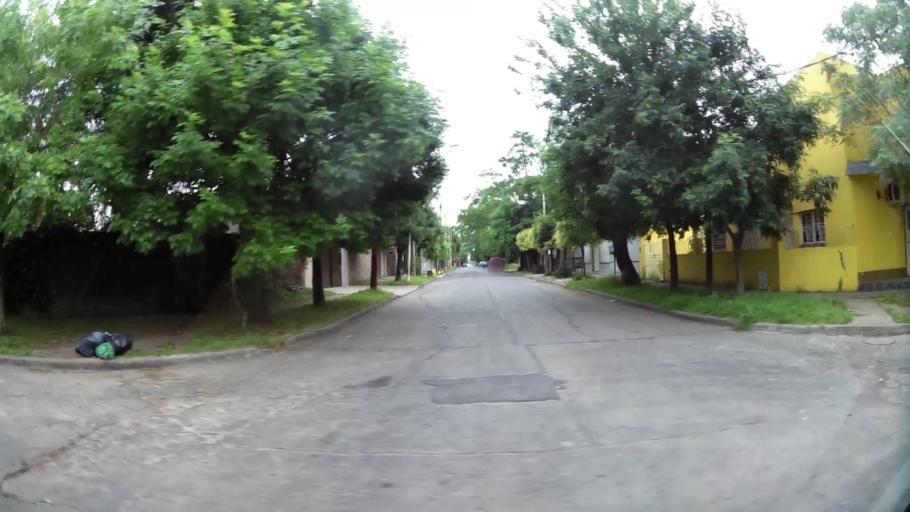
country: AR
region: Buenos Aires
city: San Justo
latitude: -34.7055
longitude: -58.5175
